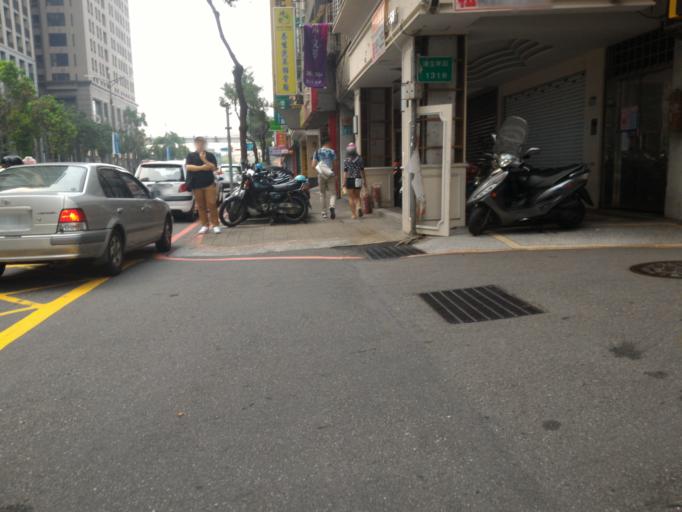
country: TW
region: Taipei
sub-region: Taipei
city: Banqiao
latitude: 25.0145
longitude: 121.4675
